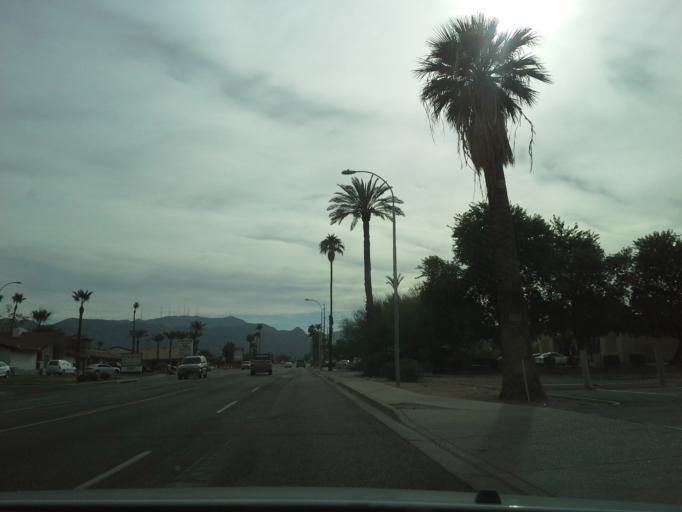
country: US
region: Arizona
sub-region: Maricopa County
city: Phoenix
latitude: 33.3828
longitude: -112.0734
